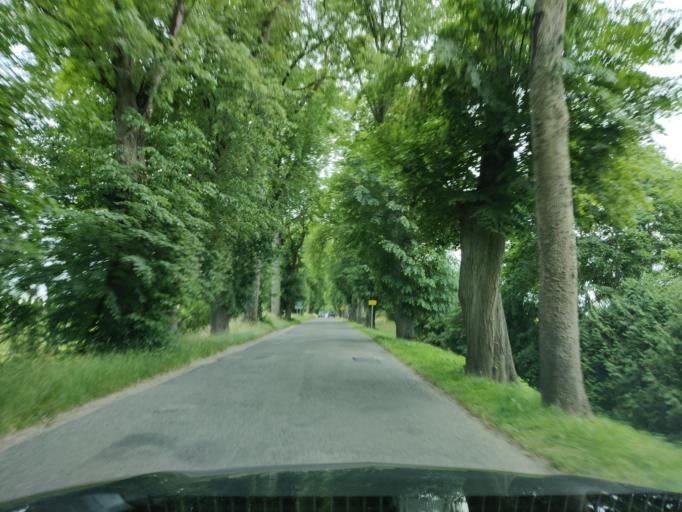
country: PL
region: Warmian-Masurian Voivodeship
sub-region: Powiat gizycki
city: Ryn
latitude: 53.9315
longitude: 21.5500
